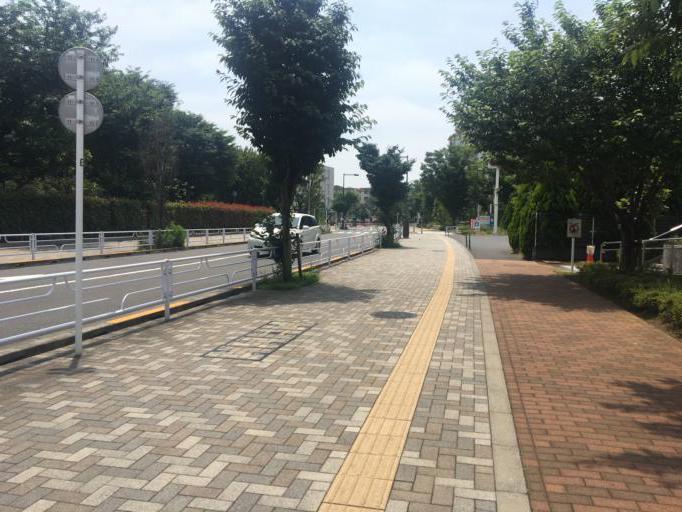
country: JP
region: Tokyo
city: Tanashicho
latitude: 35.7441
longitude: 139.5365
